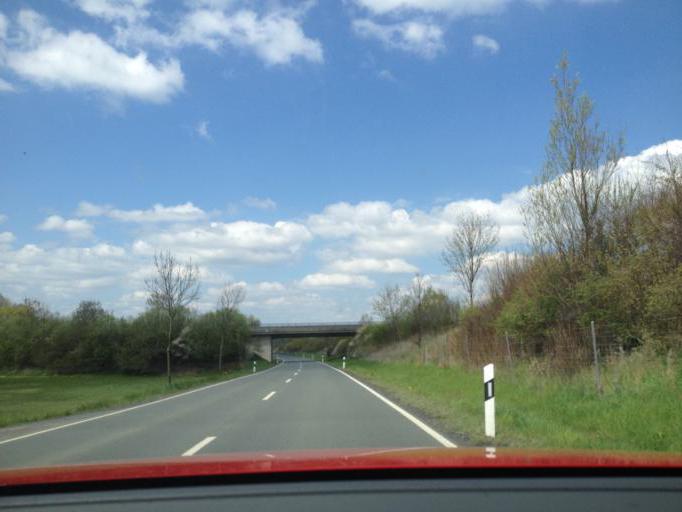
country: DE
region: Bavaria
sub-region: Upper Franconia
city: Marktredwitz
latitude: 49.9972
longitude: 12.1207
